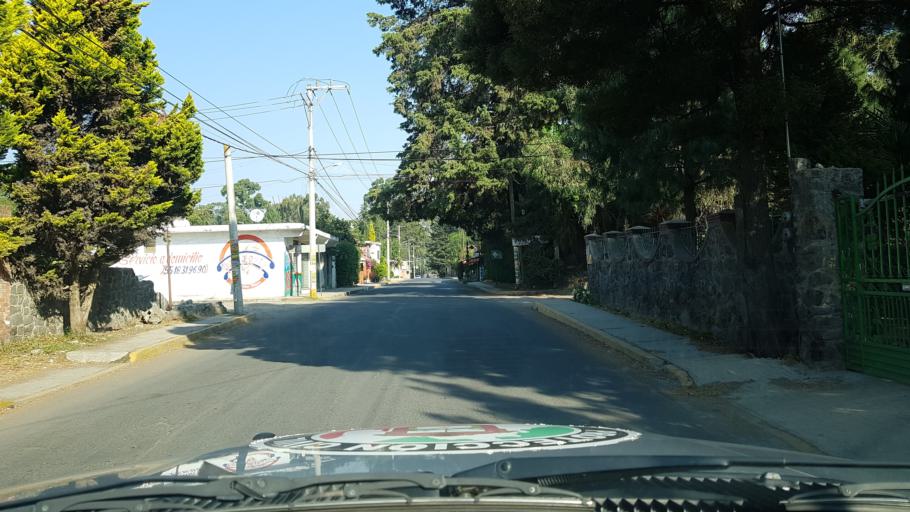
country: MX
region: Mexico
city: Ozumba de Alzate
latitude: 19.0575
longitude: -98.7757
